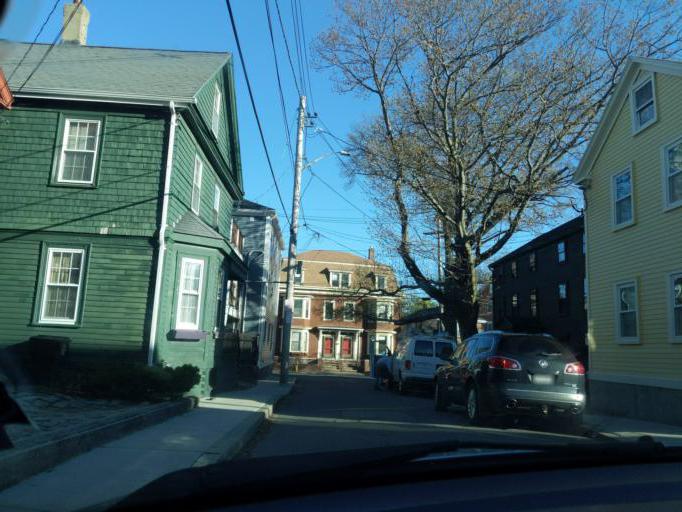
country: US
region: Massachusetts
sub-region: Essex County
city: Salem
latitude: 42.5226
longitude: -70.8864
